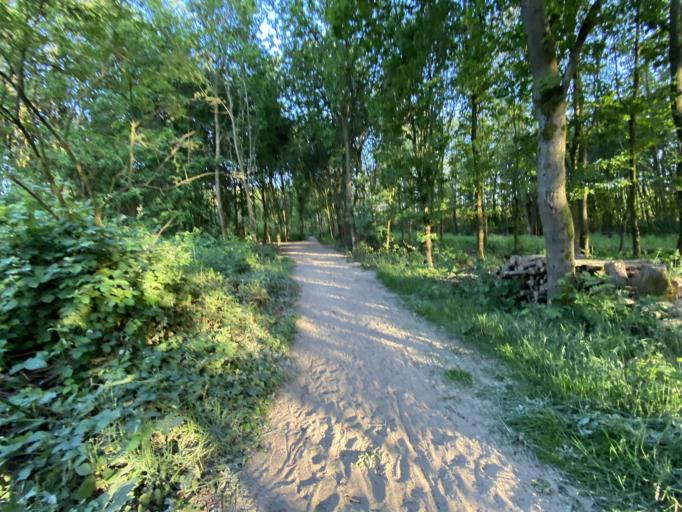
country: NL
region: North Holland
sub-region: Gemeente Diemen
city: Diemen
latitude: 52.3315
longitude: 4.9926
